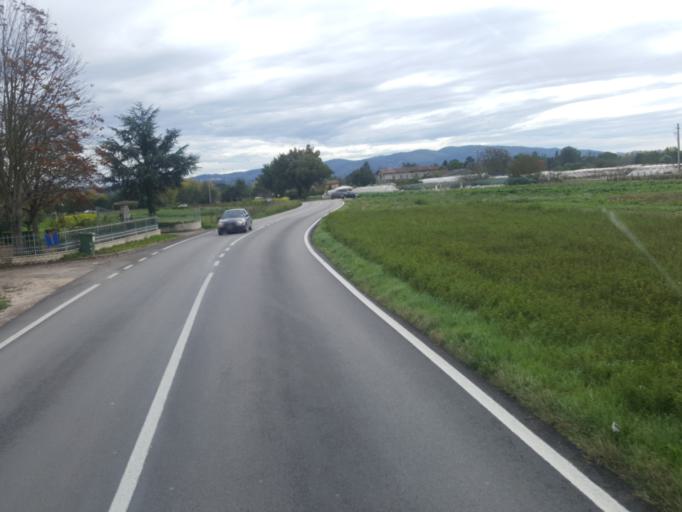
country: IT
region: Umbria
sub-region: Provincia di Perugia
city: San Martino in Campo
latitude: 43.0742
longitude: 12.4245
